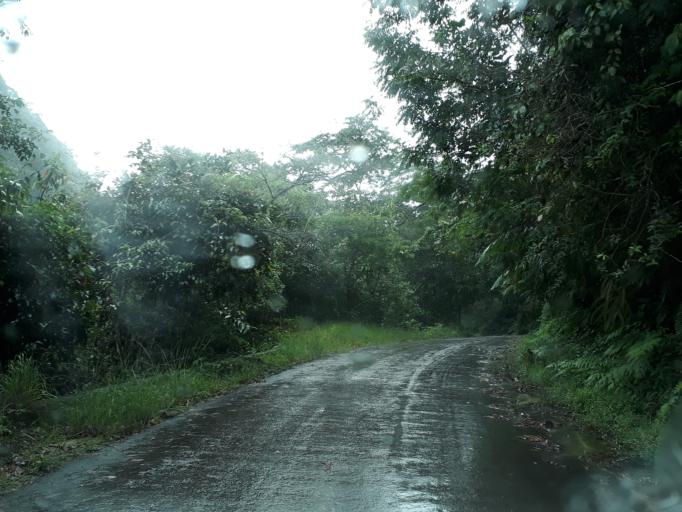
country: CO
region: Boyaca
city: Santa Maria
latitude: 4.7276
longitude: -73.3009
